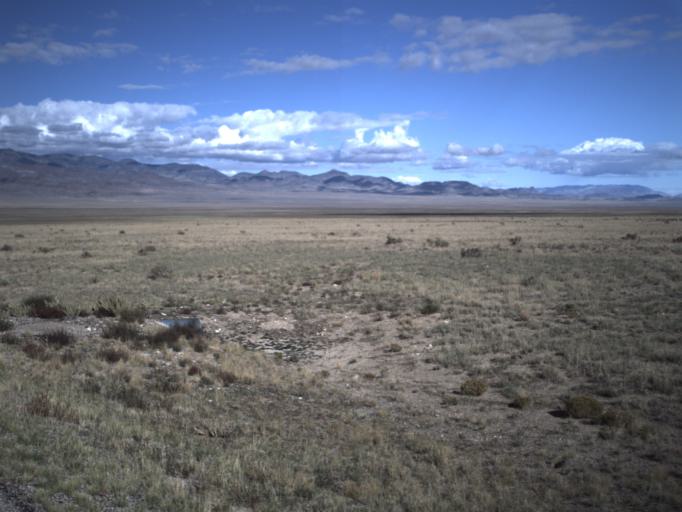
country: US
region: Utah
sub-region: Beaver County
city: Milford
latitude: 38.4536
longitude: -113.3551
